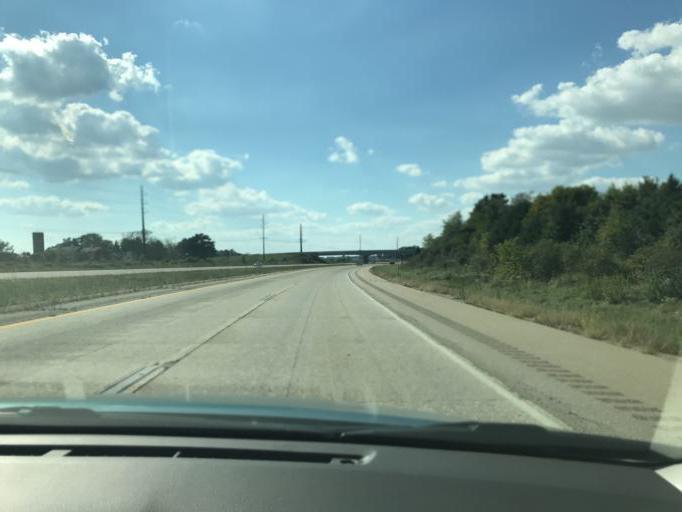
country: US
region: Wisconsin
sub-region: Walworth County
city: Delavan
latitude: 42.6123
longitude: -88.6446
